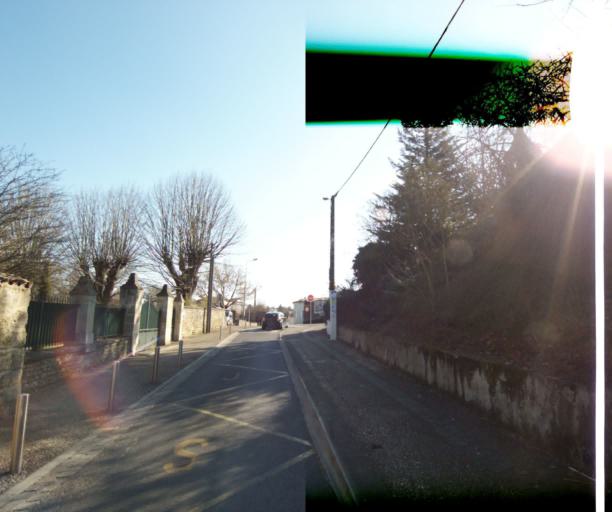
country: FR
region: Poitou-Charentes
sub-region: Departement des Deux-Sevres
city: Aiffres
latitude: 46.3265
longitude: -0.4245
